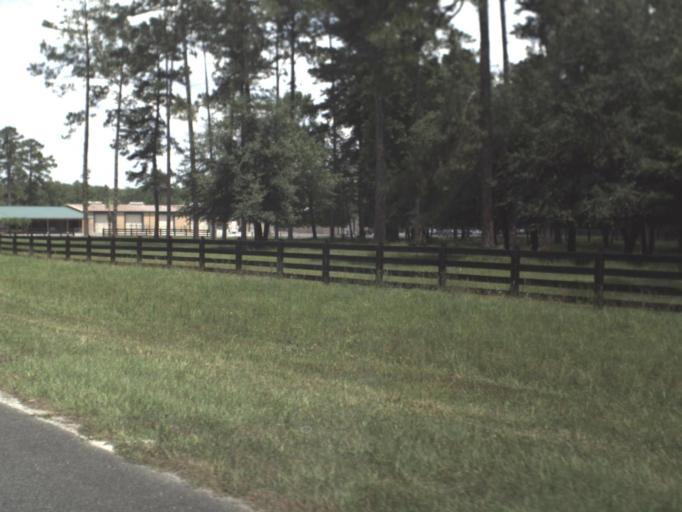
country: US
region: Florida
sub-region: Union County
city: Lake Butler
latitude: 30.0540
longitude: -82.4111
